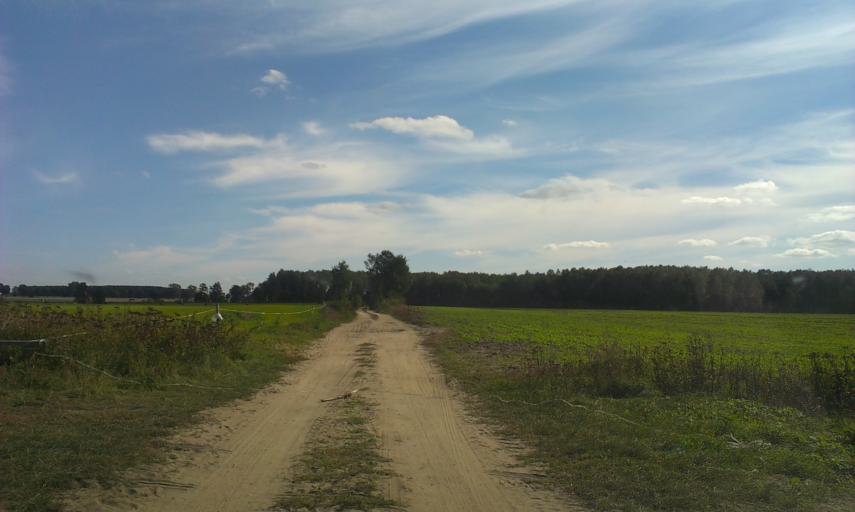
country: PL
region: Greater Poland Voivodeship
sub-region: Powiat pilski
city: Lobzenica
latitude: 53.2887
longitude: 17.1635
